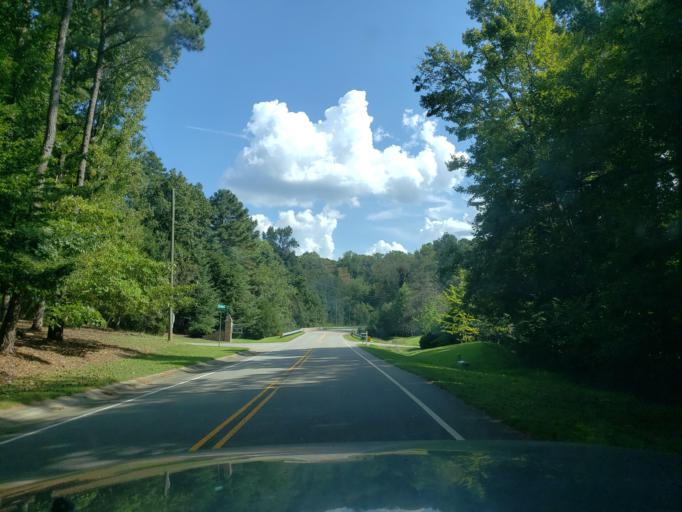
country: US
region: North Carolina
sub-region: Wake County
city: West Raleigh
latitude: 35.9274
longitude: -78.6889
